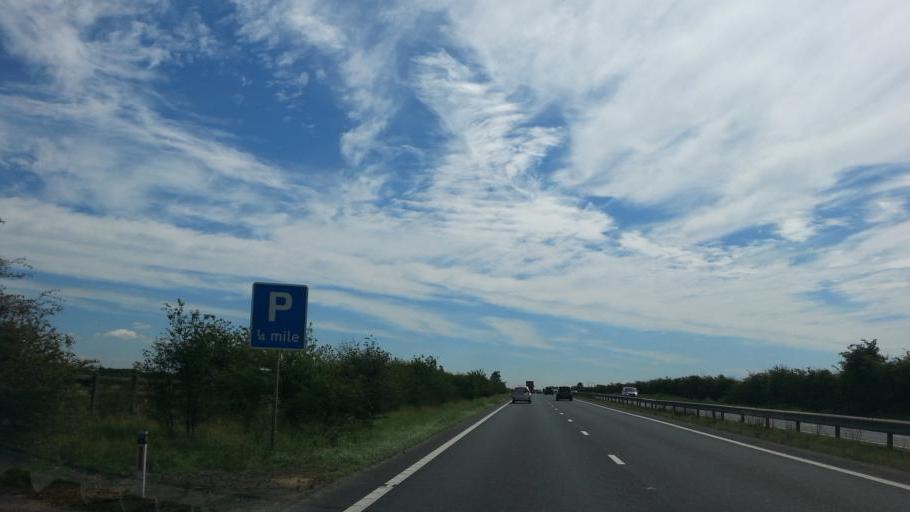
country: GB
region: England
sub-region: Cambridgeshire
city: Waterbeach
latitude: 52.2261
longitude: 0.1831
